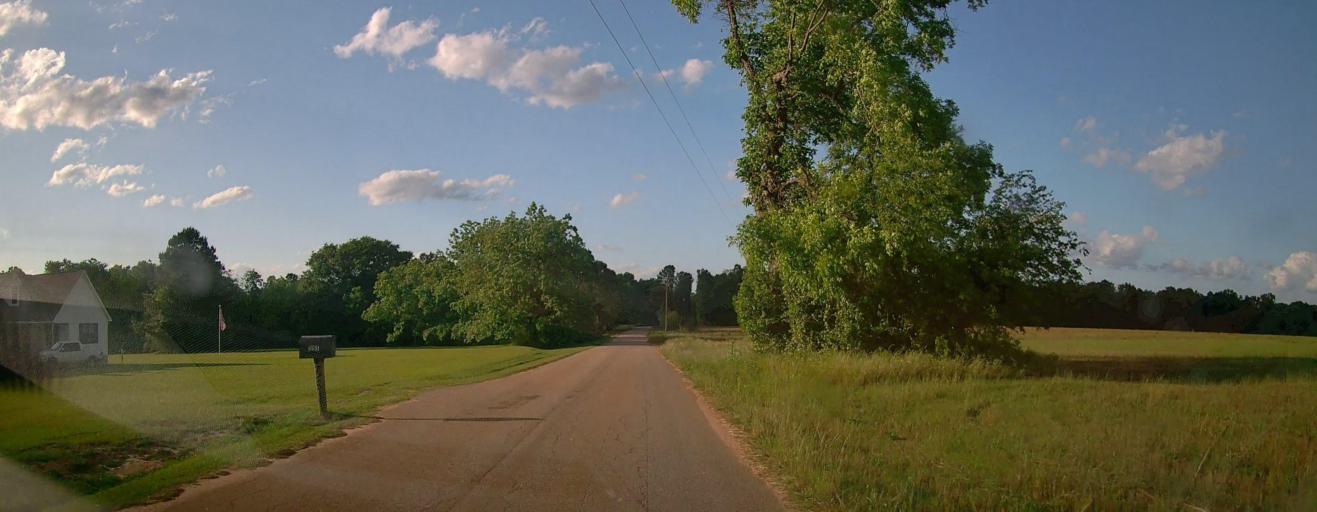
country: US
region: Georgia
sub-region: Peach County
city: Byron
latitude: 32.6112
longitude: -83.7735
